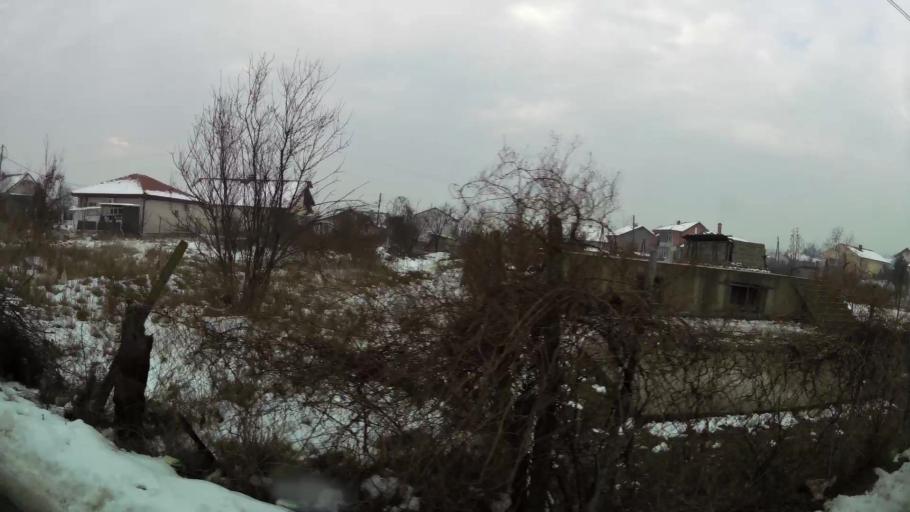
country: MK
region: Saraj
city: Saraj
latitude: 42.0401
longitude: 21.3509
